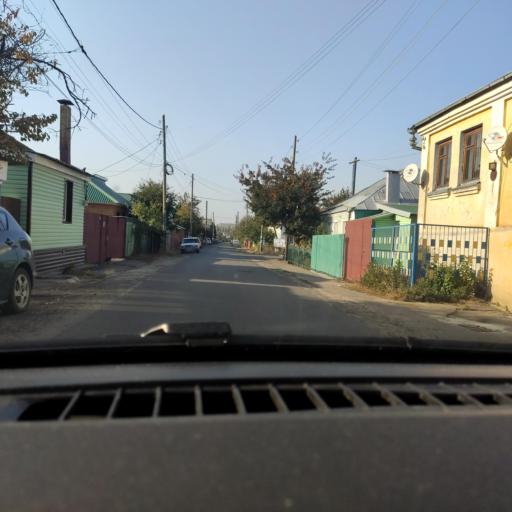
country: RU
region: Voronezj
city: Voronezh
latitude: 51.6286
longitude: 39.1701
